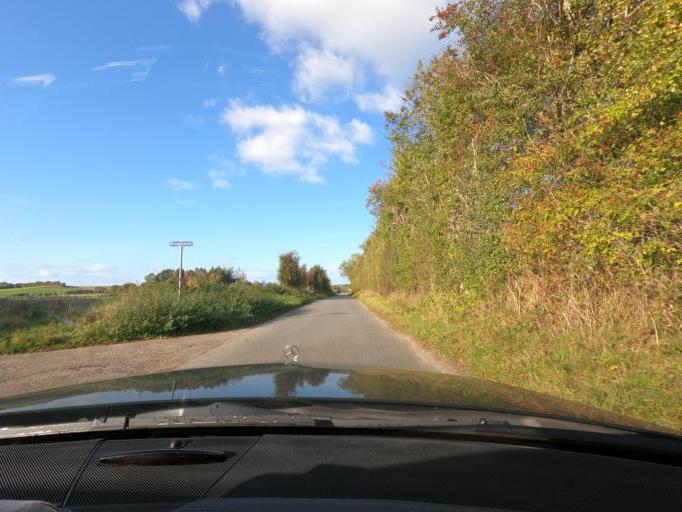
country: DK
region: South Denmark
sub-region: Sonderborg Kommune
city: Broager
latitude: 54.8894
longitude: 9.7034
